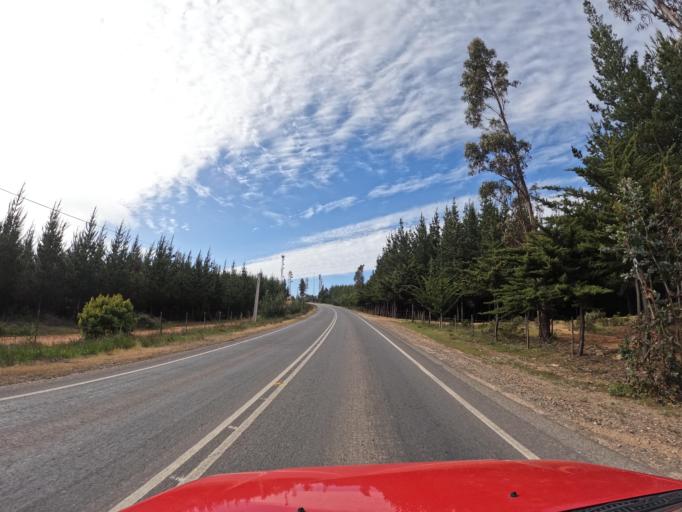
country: CL
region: O'Higgins
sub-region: Provincia de Colchagua
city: Santa Cruz
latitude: -34.3377
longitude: -71.8751
